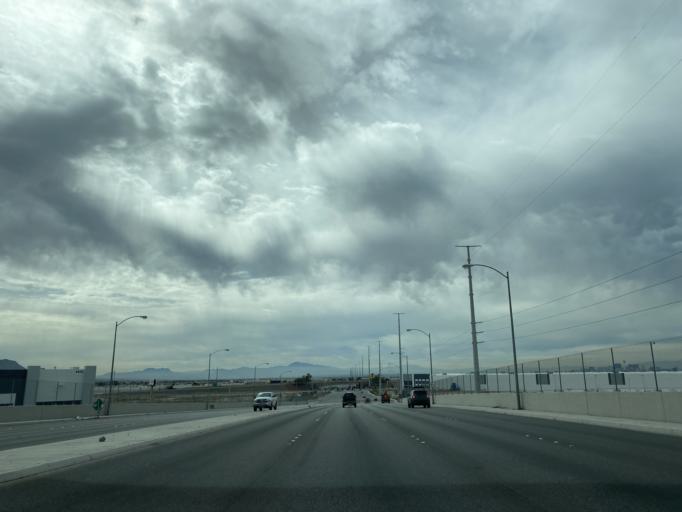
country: US
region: Nevada
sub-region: Clark County
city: Nellis Air Force Base
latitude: 36.2652
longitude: -115.0799
